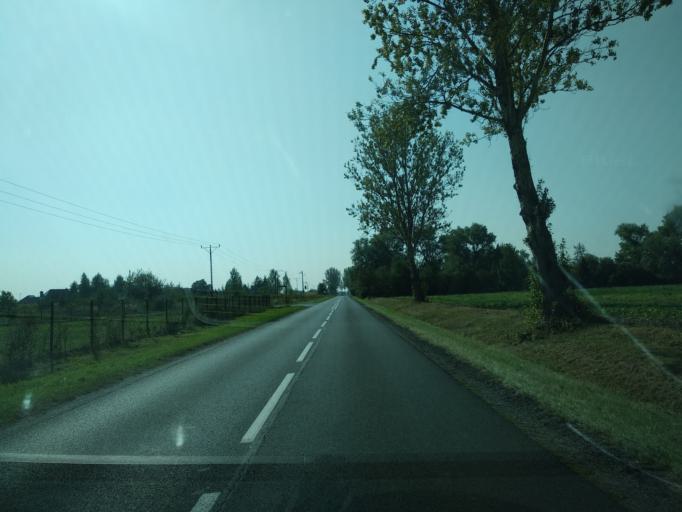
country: PL
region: Lower Silesian Voivodeship
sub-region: Powiat wroclawski
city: Zerniki Wroclawskie
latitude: 51.0280
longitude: 17.0335
